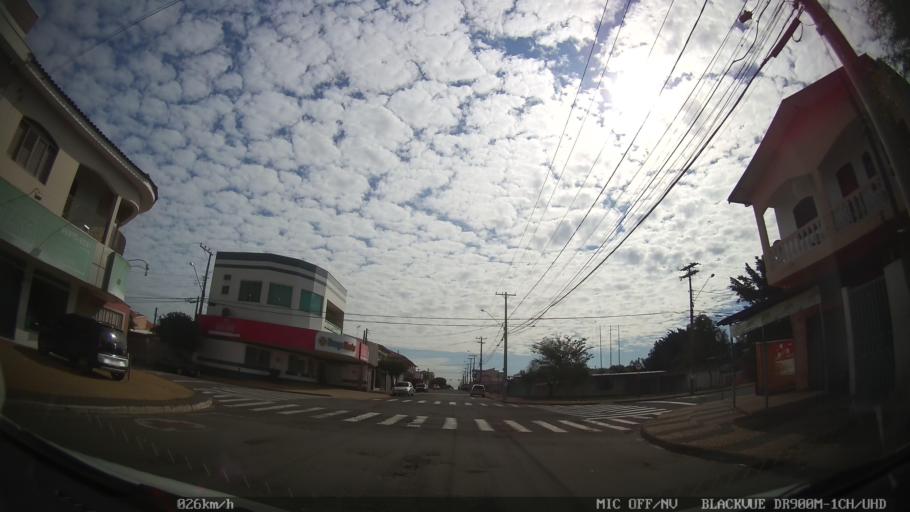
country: BR
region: Sao Paulo
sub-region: Santa Barbara D'Oeste
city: Santa Barbara d'Oeste
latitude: -22.7709
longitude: -47.3912
